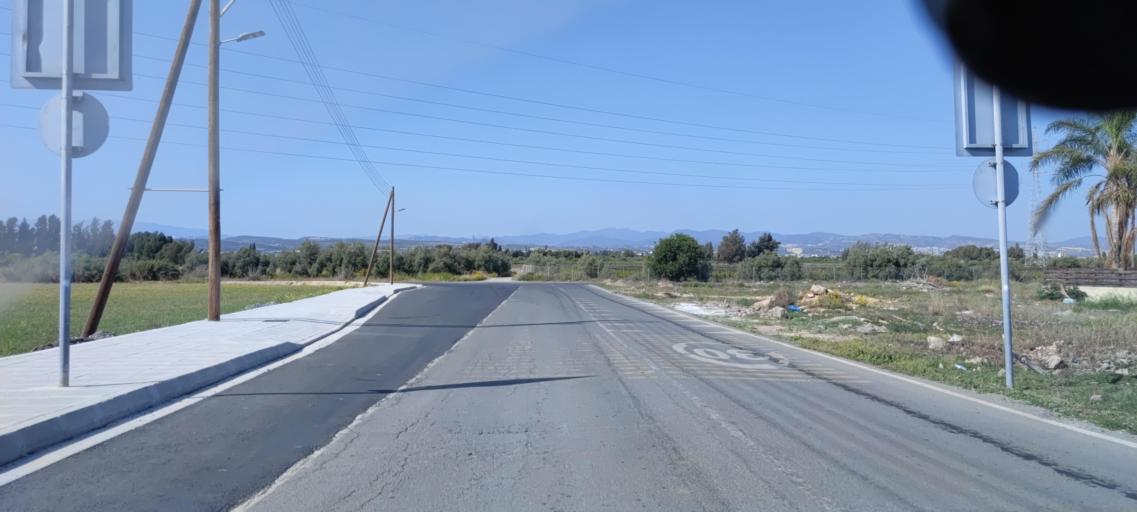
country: CY
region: Larnaka
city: Kolossi
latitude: 34.6625
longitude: 32.9579
